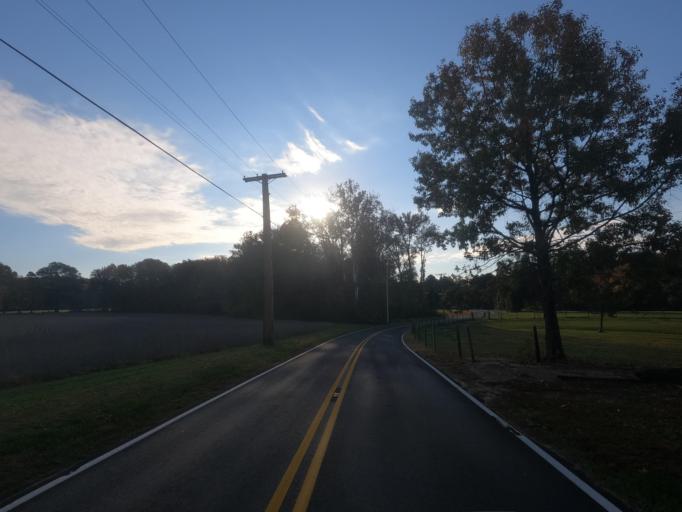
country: US
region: Maryland
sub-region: Saint Mary's County
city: Golden Beach
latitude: 38.4981
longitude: -76.6360
